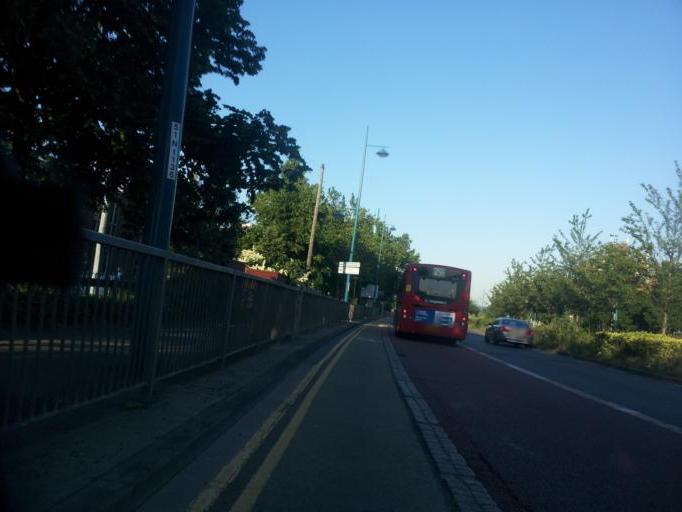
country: GB
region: England
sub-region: Greater London
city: Woolwich
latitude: 51.4912
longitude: 0.0786
